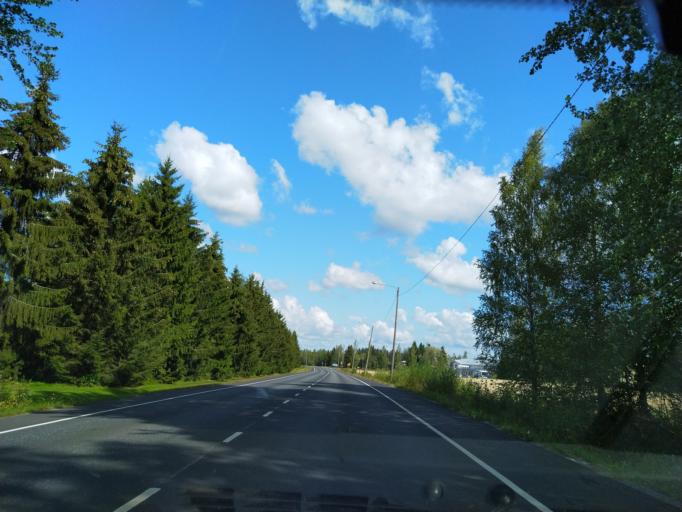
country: FI
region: Satakunta
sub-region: Pori
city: Huittinen
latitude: 61.1767
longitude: 22.7120
